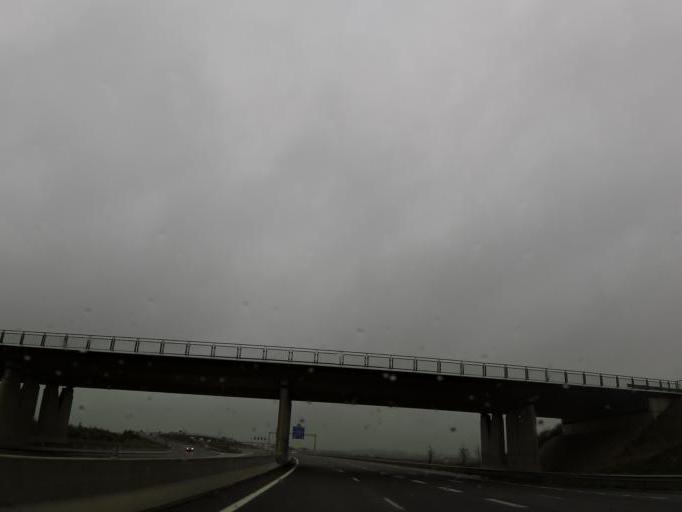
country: FR
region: Champagne-Ardenne
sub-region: Departement de la Marne
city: Tinqueux
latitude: 49.2399
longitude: 3.9683
